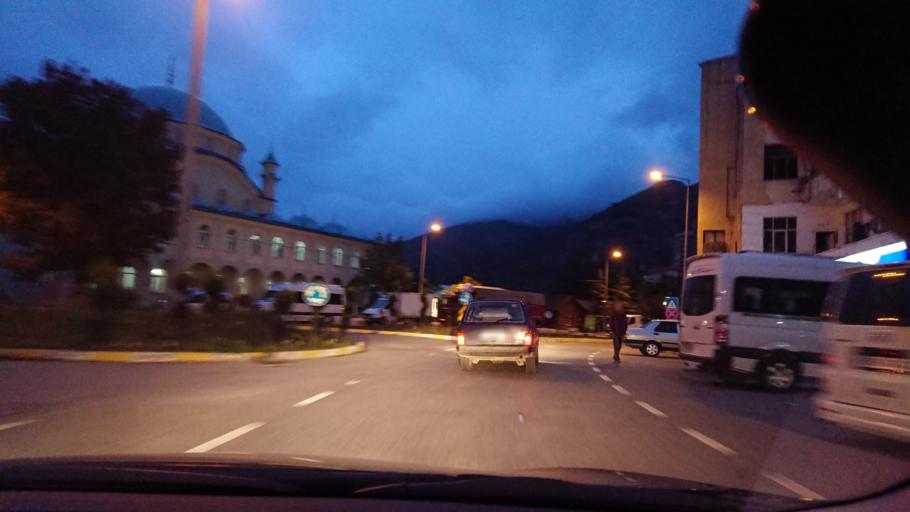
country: TR
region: Gumushane
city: Kurtun
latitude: 40.6695
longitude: 39.1395
